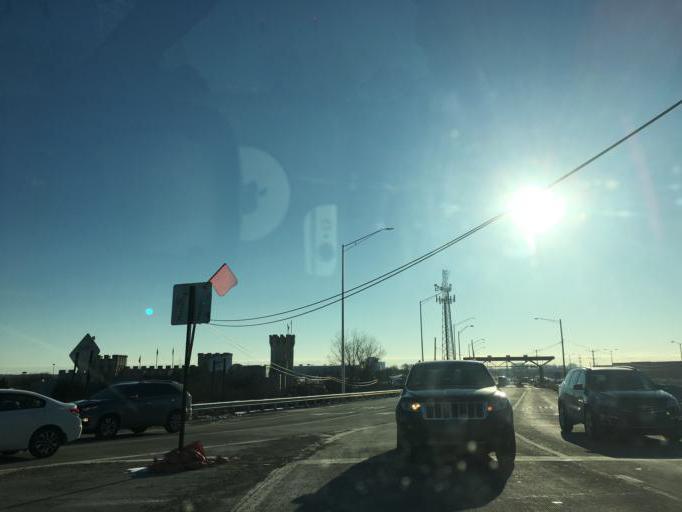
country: US
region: Illinois
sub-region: Cook County
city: Hoffman Estates
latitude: 42.0646
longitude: -88.0793
